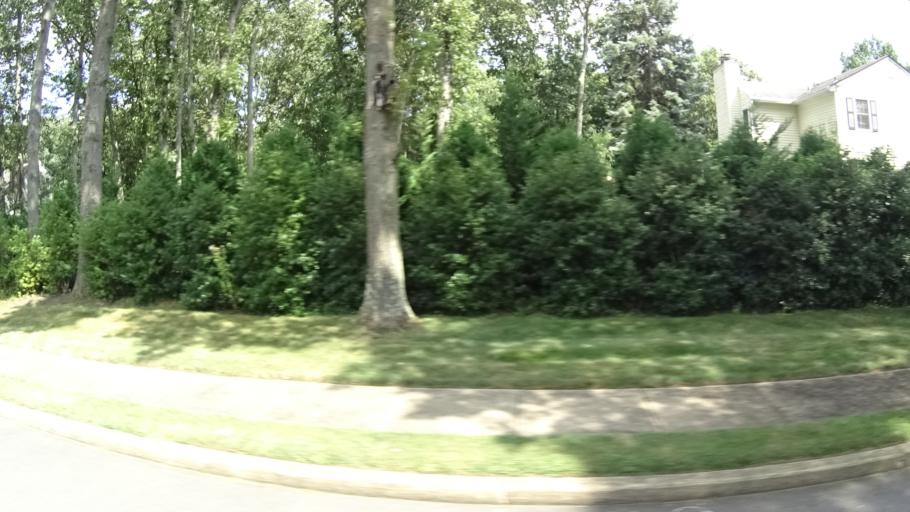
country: US
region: New Jersey
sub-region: Monmouth County
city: Brielle
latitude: 40.1104
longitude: -74.0865
